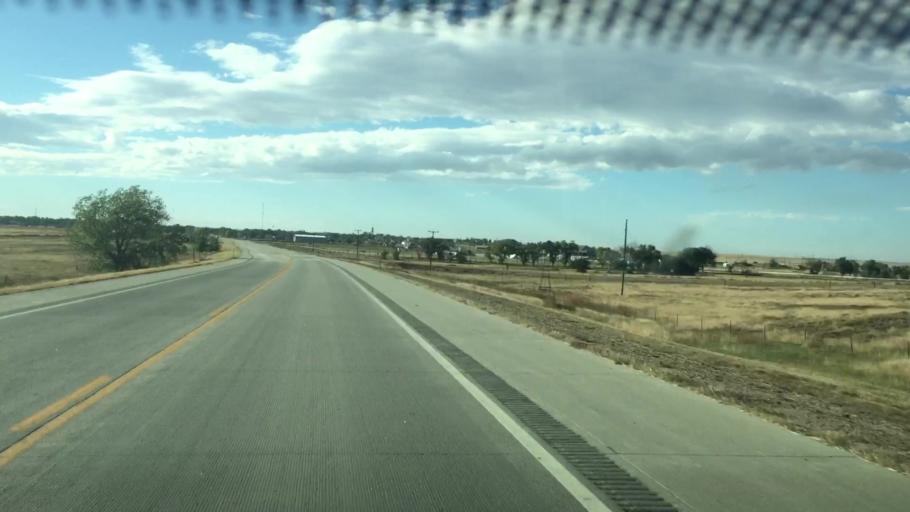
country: US
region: Colorado
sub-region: Lincoln County
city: Hugo
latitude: 39.1267
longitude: -103.4477
